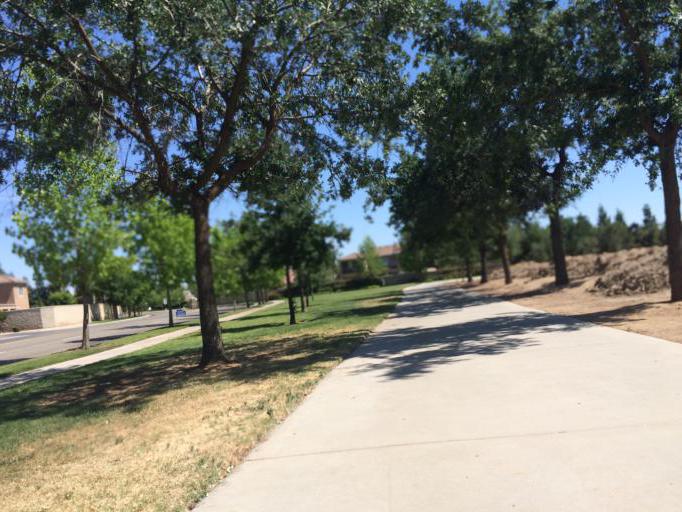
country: US
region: California
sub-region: Fresno County
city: Clovis
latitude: 36.8640
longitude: -119.6748
